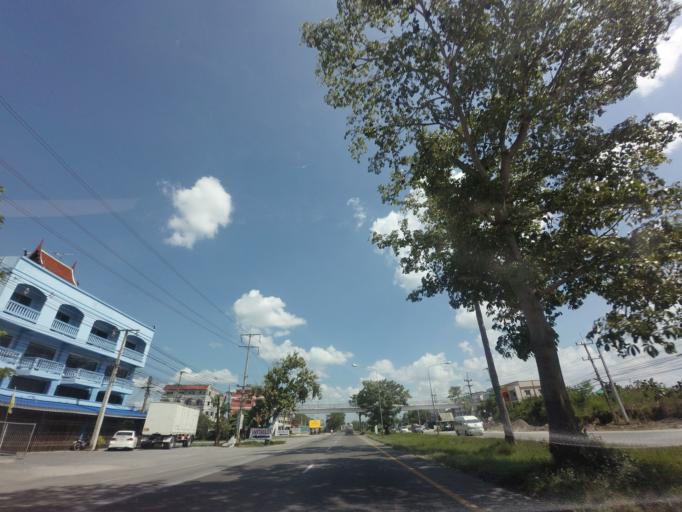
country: TH
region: Chon Buri
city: Ban Bueng
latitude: 13.3020
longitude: 101.1430
